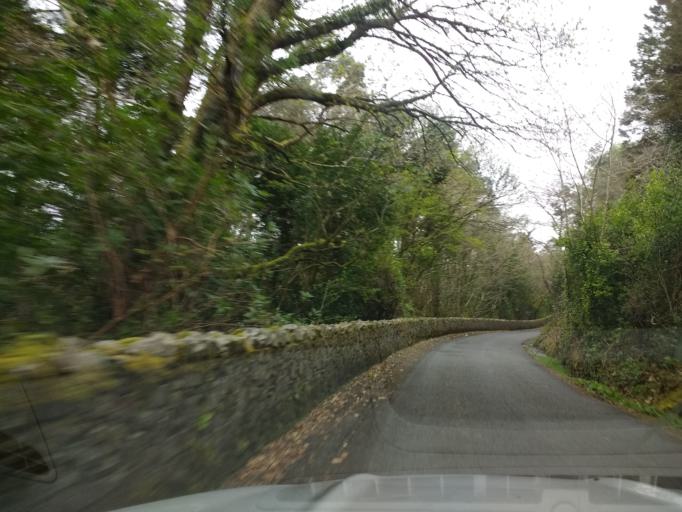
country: IE
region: Ulster
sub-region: County Donegal
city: Buncrana
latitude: 55.2189
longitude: -7.6116
